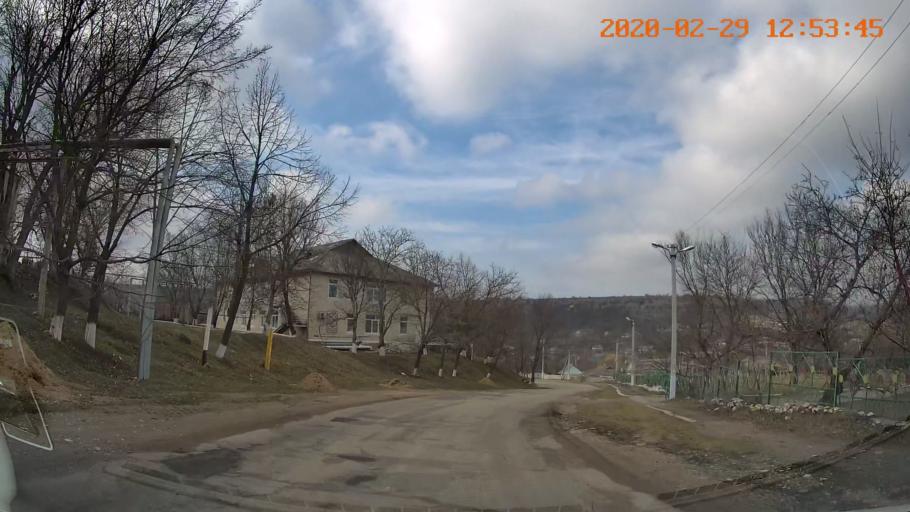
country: MD
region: Telenesti
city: Camenca
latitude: 48.1051
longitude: 28.7319
